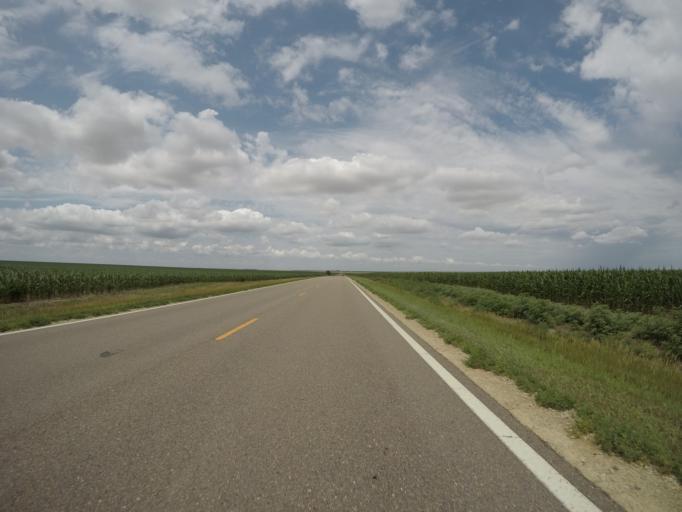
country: US
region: Kansas
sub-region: Rawlins County
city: Atwood
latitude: 39.6735
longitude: -101.0566
